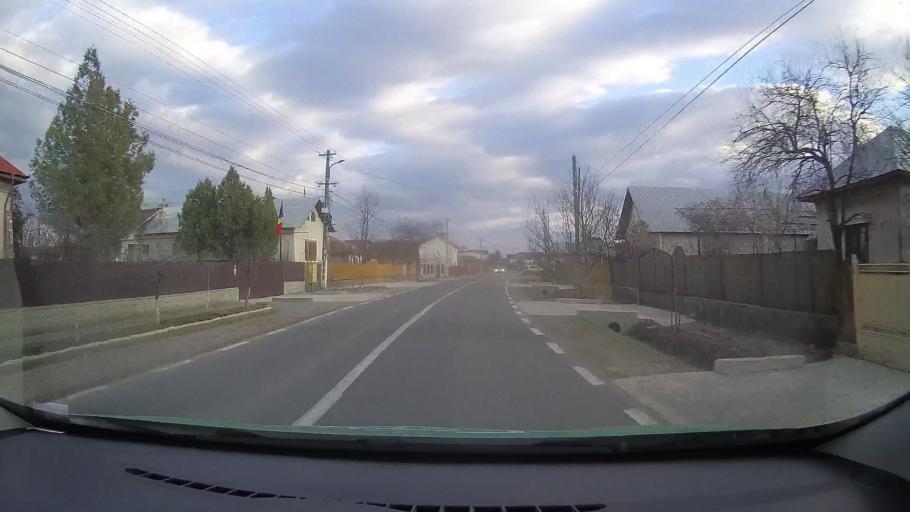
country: RO
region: Dambovita
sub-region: Comuna I. L. Caragiale
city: Ghirdoveni
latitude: 44.9366
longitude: 25.6826
